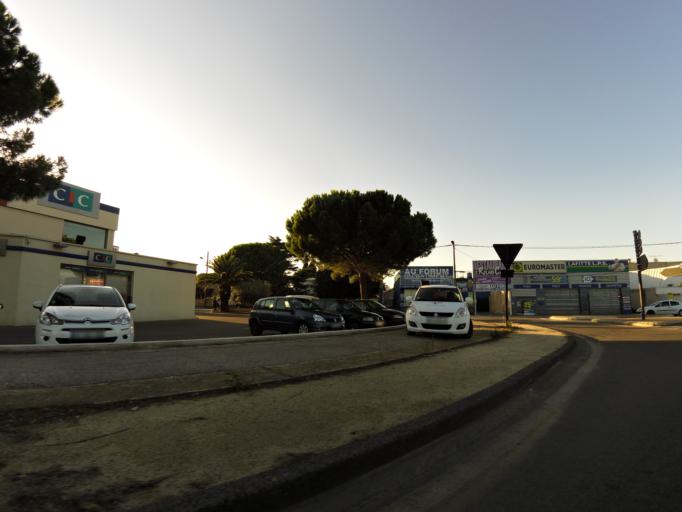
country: FR
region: Languedoc-Roussillon
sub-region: Departement du Gard
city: Nimes
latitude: 43.8142
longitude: 4.3343
